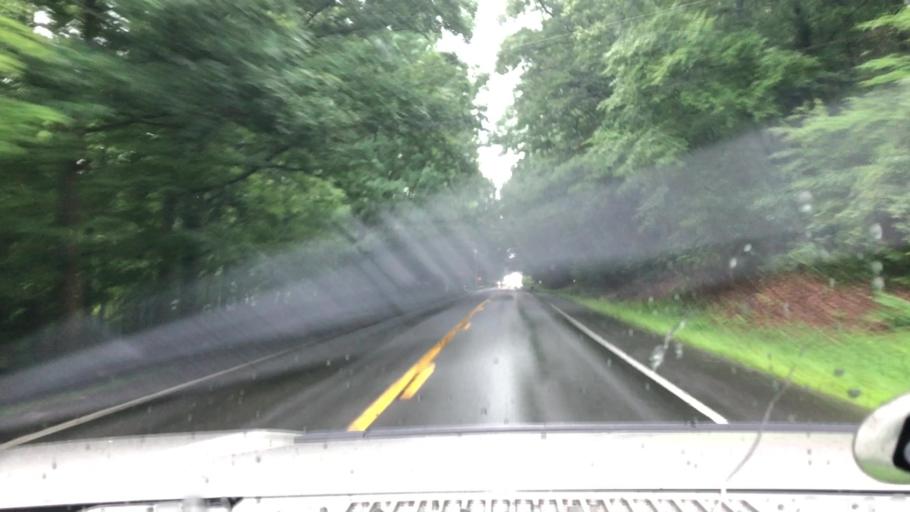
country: US
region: New York
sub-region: Greene County
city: Palenville
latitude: 42.1732
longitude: -73.9881
